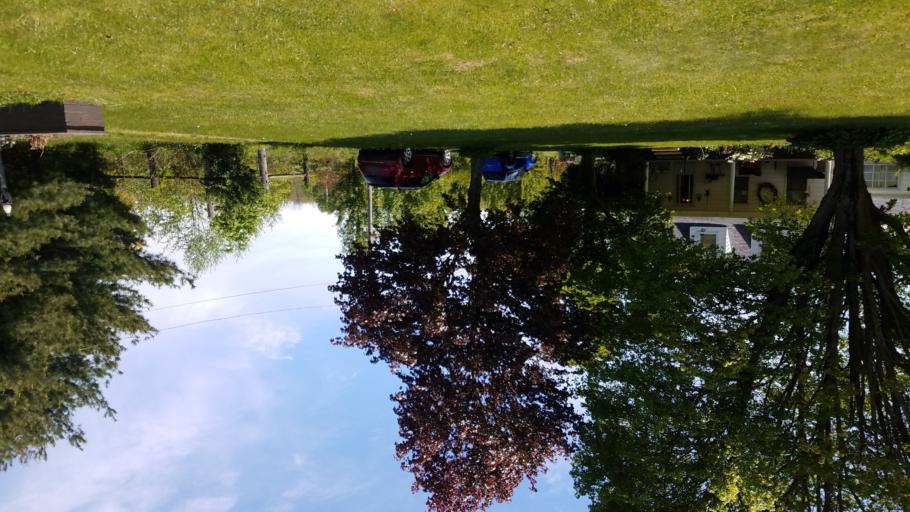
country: US
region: Ohio
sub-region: Knox County
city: Gambier
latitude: 40.4074
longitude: -82.4053
